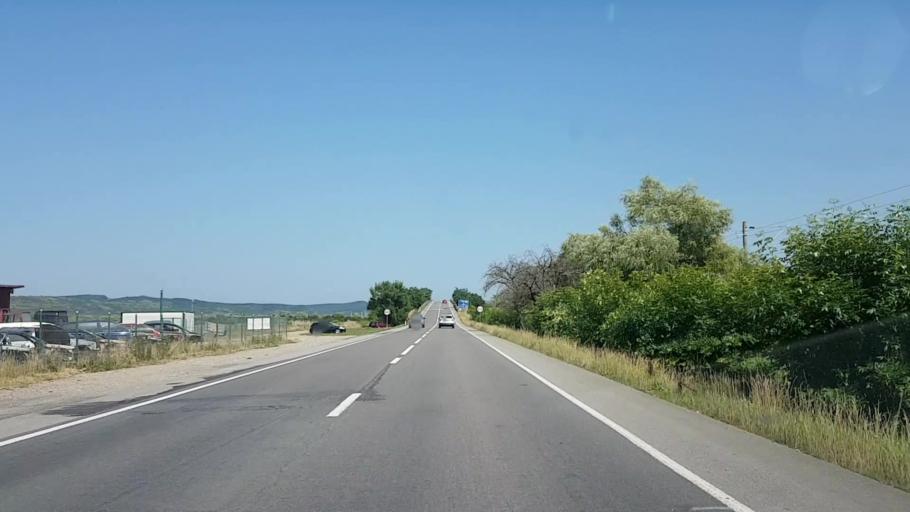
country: RO
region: Bistrita-Nasaud
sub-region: Comuna Sintereag
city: Cociu
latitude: 47.1831
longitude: 24.2267
